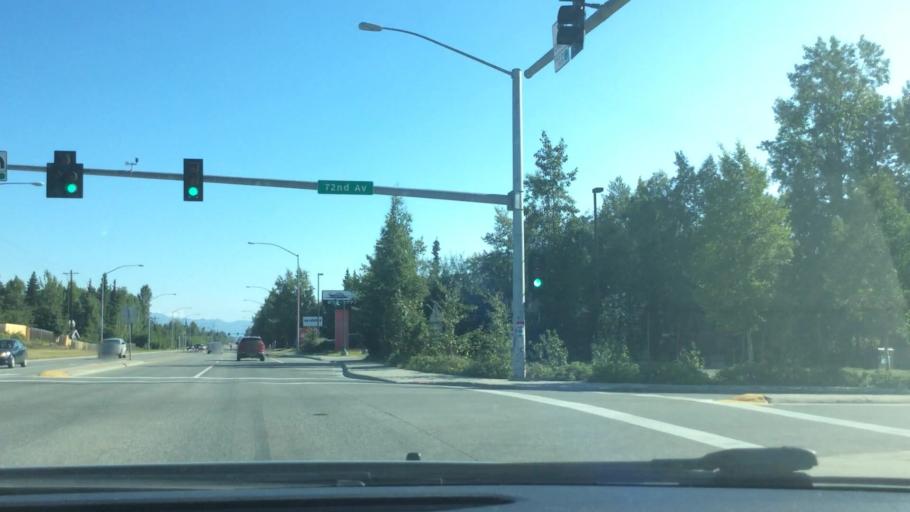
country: US
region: Alaska
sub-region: Anchorage Municipality
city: Anchorage
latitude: 61.1558
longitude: -149.8344
